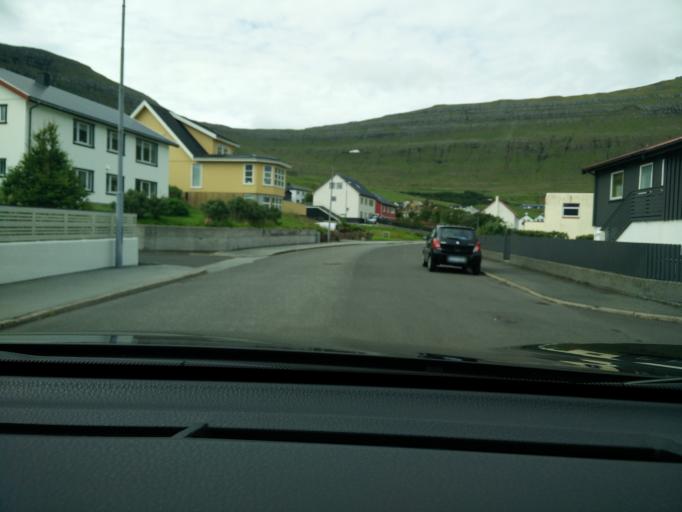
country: FO
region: Eysturoy
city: Eystur
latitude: 62.2096
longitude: -6.6998
